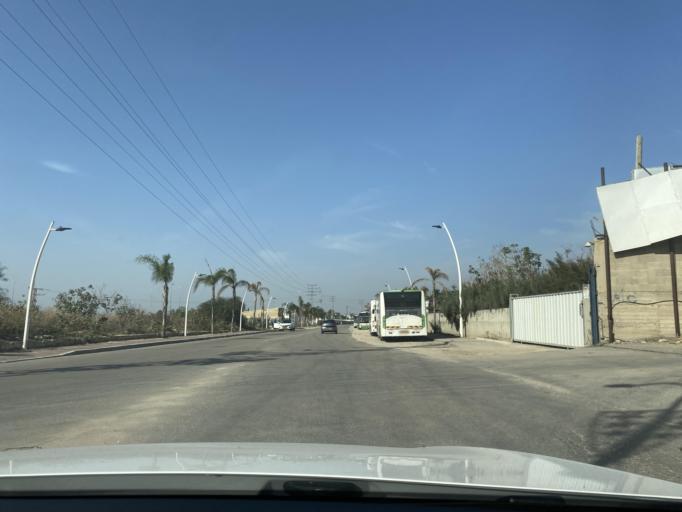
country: IL
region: Central District
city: Jaljulya
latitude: 32.1353
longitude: 34.9630
